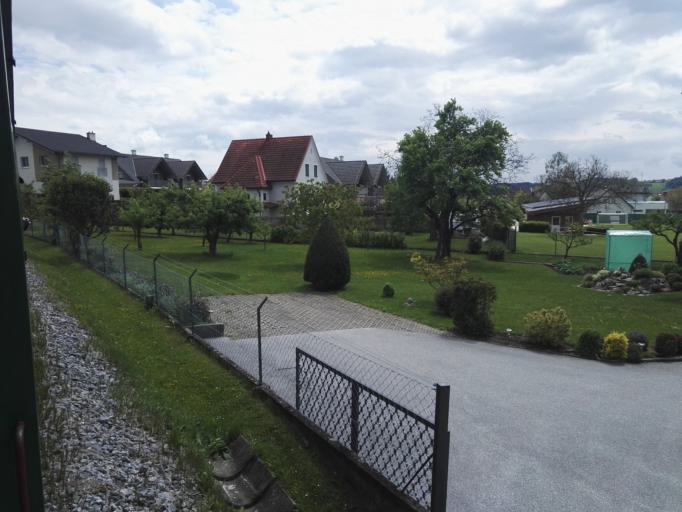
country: AT
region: Styria
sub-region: Politischer Bezirk Weiz
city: Krottendorf
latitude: 47.2152
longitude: 15.6414
